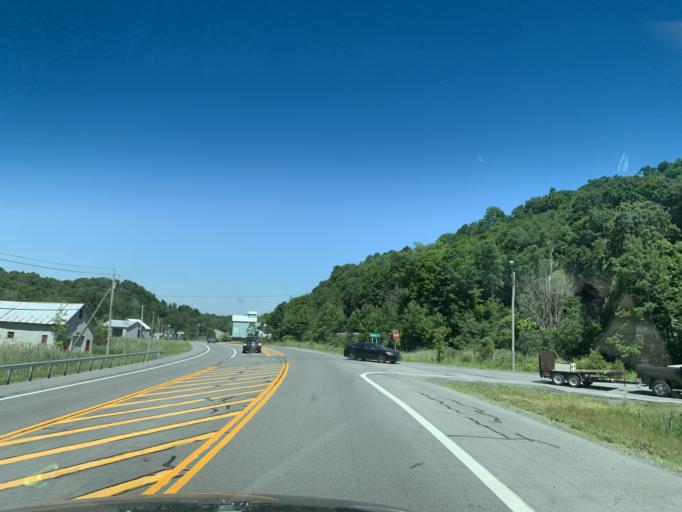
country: US
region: New York
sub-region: Oneida County
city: Chadwicks
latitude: 42.9561
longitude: -75.2412
